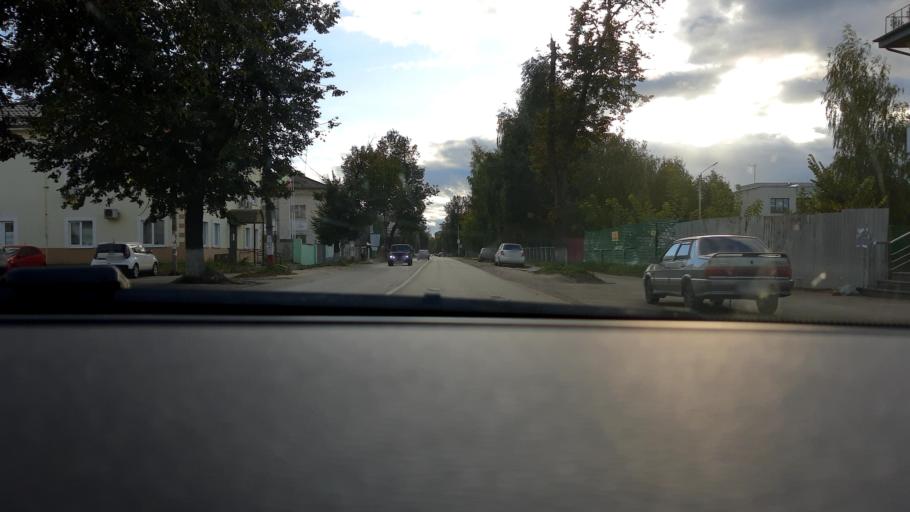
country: RU
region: Nizjnij Novgorod
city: Novaya Balakhna
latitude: 56.4911
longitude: 43.6081
